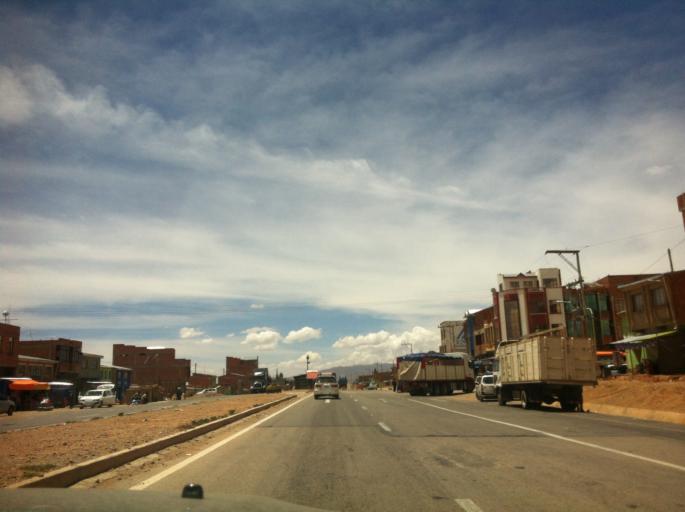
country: BO
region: La Paz
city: Eucaliptus
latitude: -17.4391
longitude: -67.5171
